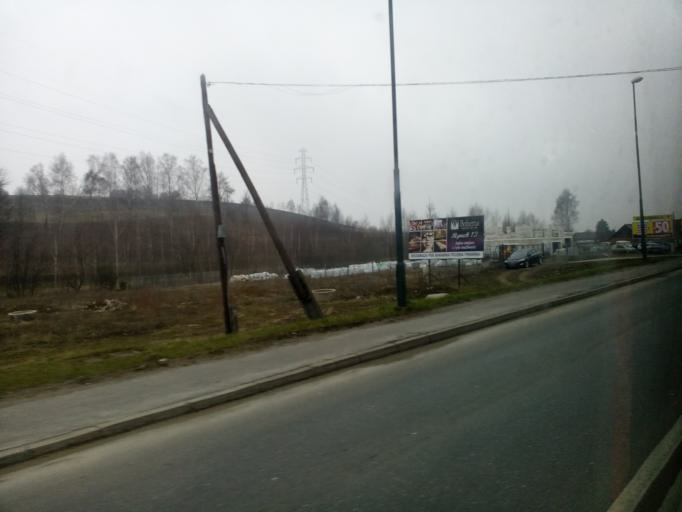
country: PL
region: Lesser Poland Voivodeship
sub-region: Powiat nowosadecki
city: Stary Sacz
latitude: 49.5764
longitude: 20.6637
